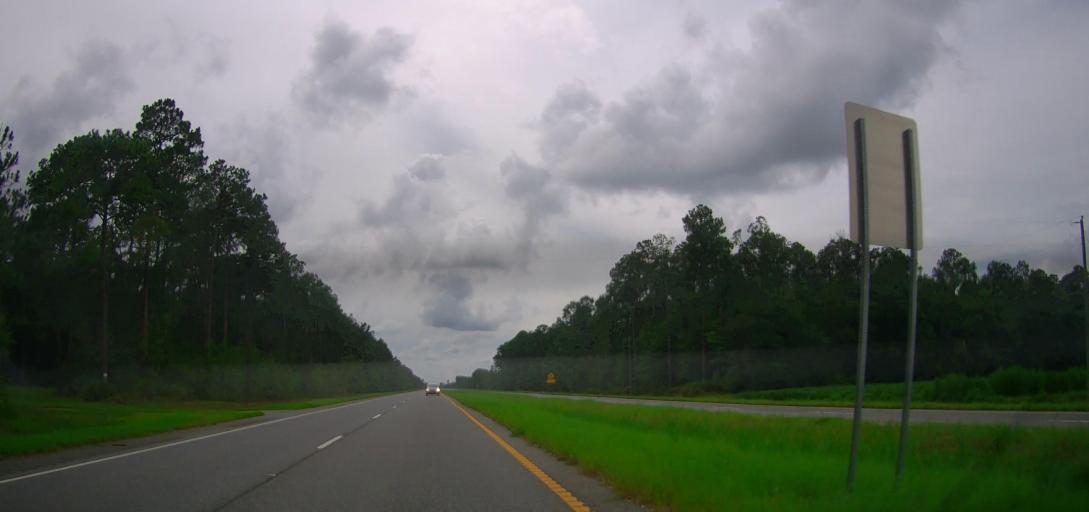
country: US
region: Georgia
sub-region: Wayne County
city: Jesup
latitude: 31.6695
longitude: -82.0530
